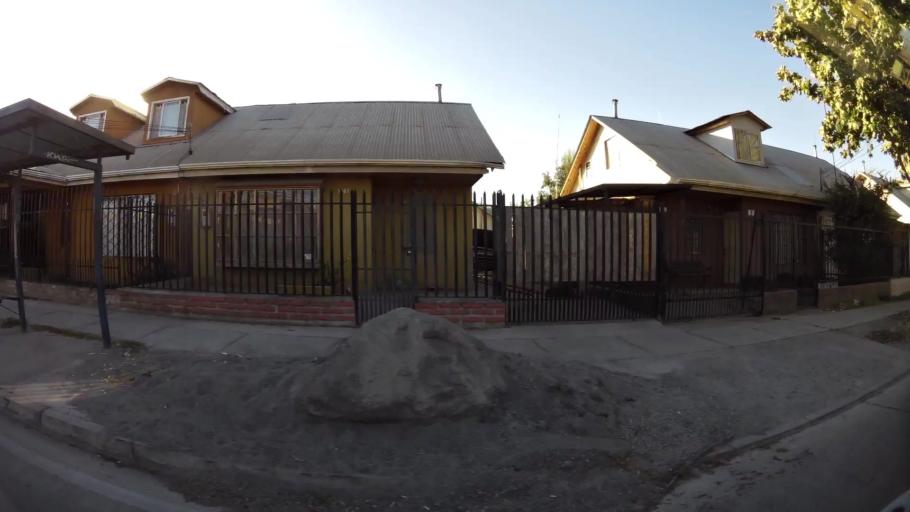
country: CL
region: O'Higgins
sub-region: Provincia de Cachapoal
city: Rancagua
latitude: -34.1766
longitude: -70.7654
